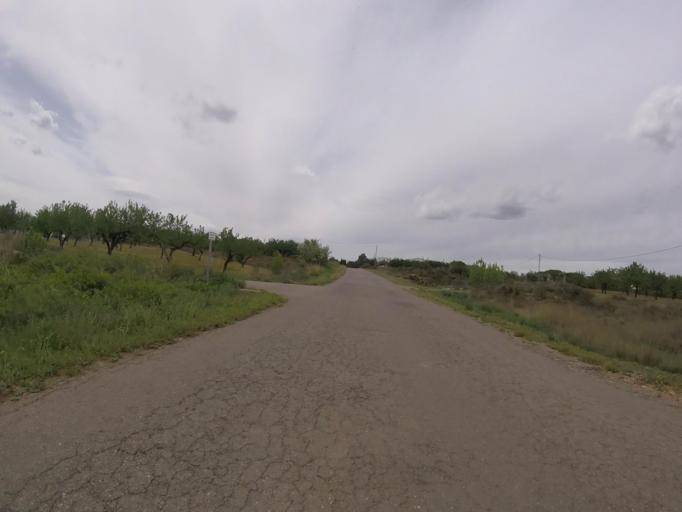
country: ES
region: Valencia
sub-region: Provincia de Castello
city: Benlloch
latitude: 40.1773
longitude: -0.0061
